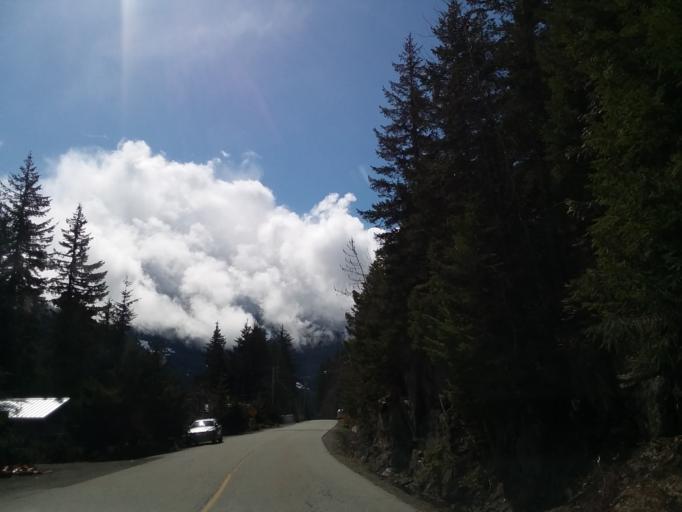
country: CA
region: British Columbia
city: Whistler
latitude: 50.1178
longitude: -122.9864
